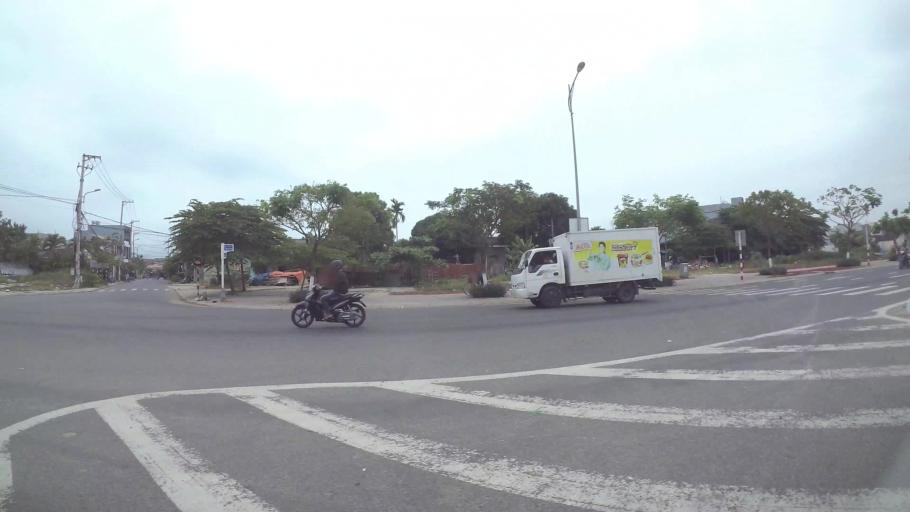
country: VN
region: Da Nang
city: Lien Chieu
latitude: 16.0695
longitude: 108.1672
